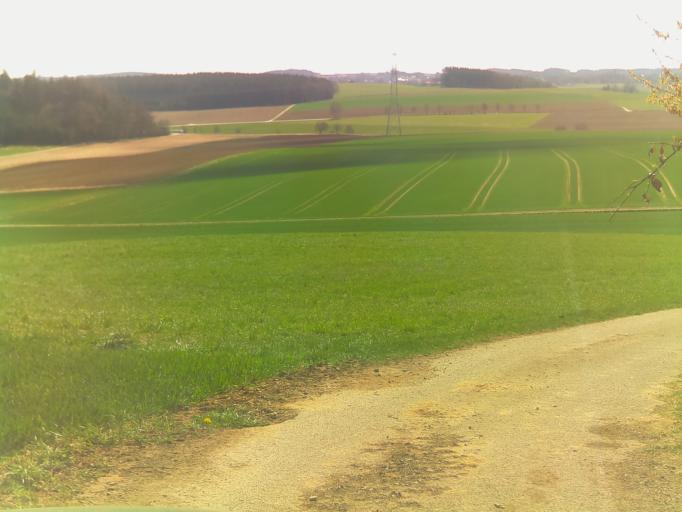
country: DE
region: Bavaria
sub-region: Swabia
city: Aindling
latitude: 48.5218
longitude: 10.9883
